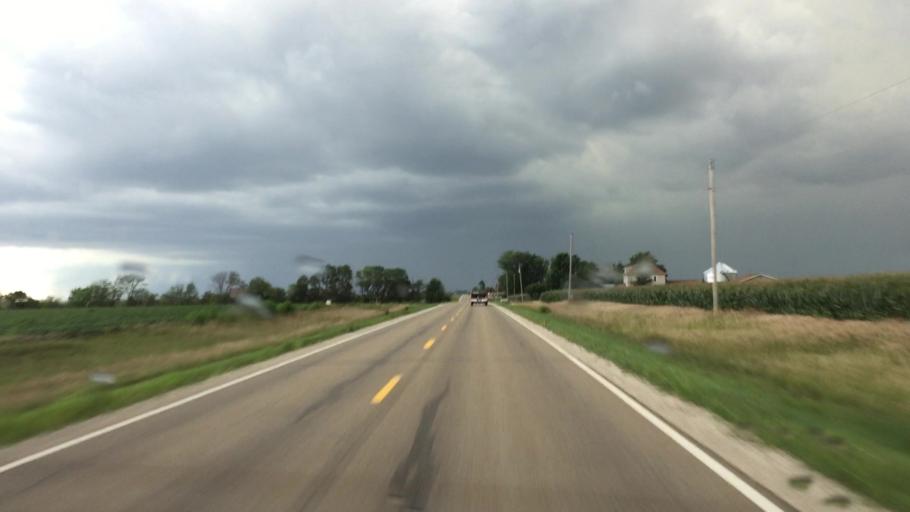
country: US
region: Iowa
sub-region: Henry County
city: New London
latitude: 40.7843
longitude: -91.5028
